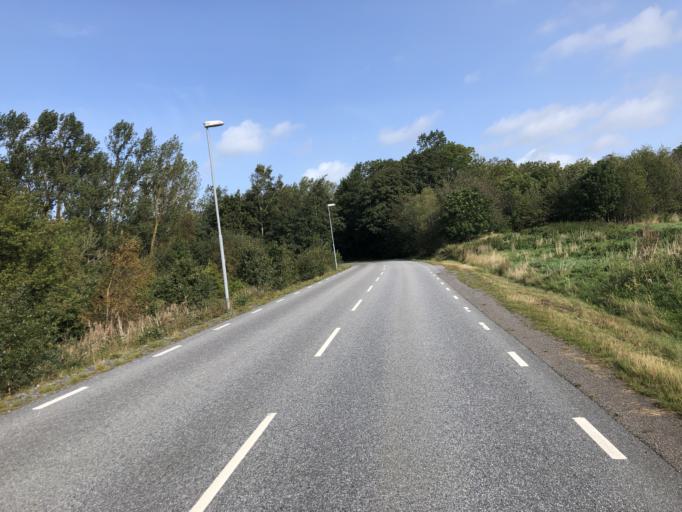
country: SE
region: Vaestra Goetaland
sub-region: Goteborg
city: Torslanda
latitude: 57.7326
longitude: 11.8441
